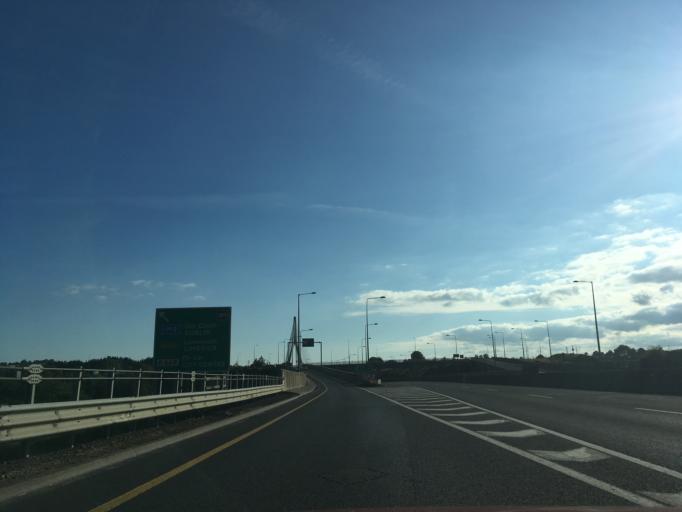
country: IE
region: Munster
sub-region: Waterford
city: Waterford
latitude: 52.2847
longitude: -7.1412
